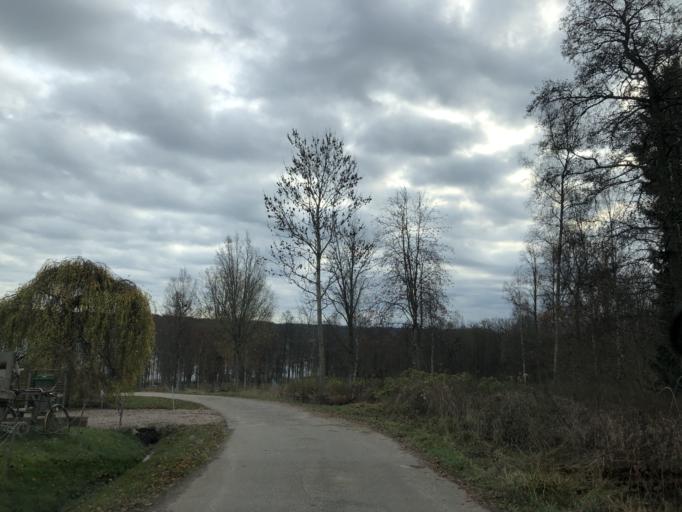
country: SE
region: Vaestra Goetaland
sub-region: Ulricehamns Kommun
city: Ulricehamn
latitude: 57.7158
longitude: 13.3640
